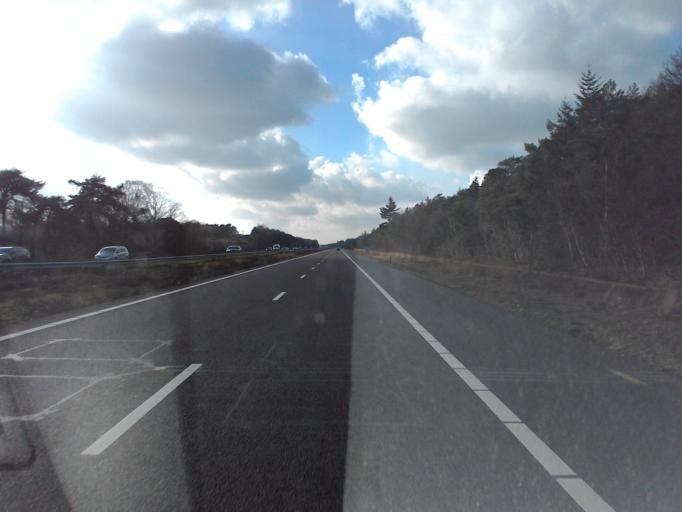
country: NL
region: North Brabant
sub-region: Gemeente Veldhoven
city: Oerle
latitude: 51.3907
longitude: 5.3684
